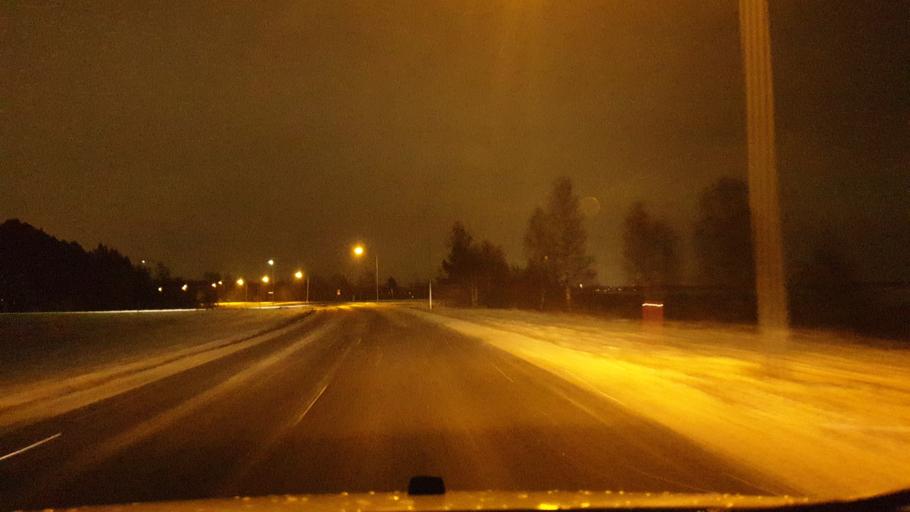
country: FI
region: Northern Ostrobothnia
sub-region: Oulu
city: Oulu
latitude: 64.9837
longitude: 25.4468
